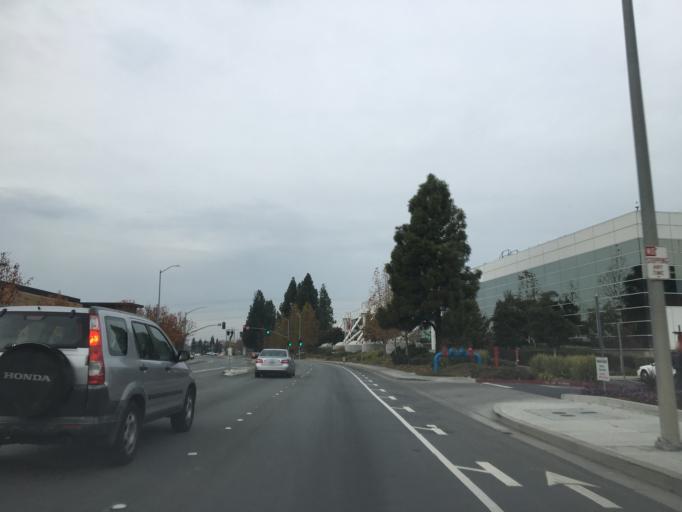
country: US
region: California
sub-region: Alameda County
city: Fremont
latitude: 37.5109
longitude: -121.9403
